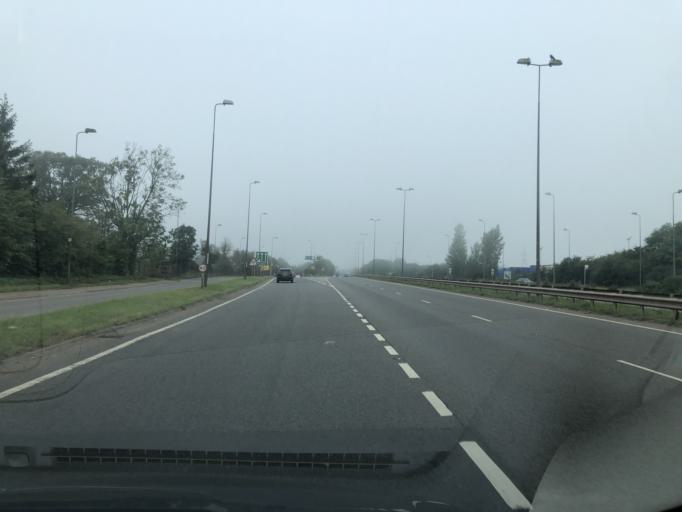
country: GB
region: England
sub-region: Solihull
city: Hampton in Arden
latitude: 52.4455
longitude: -1.7024
